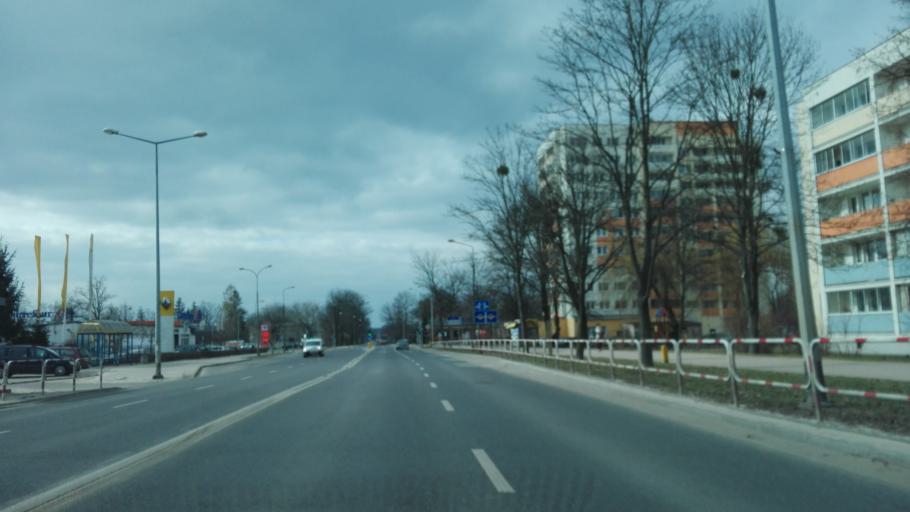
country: PL
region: Lublin Voivodeship
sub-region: Powiat pulawski
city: Pulawy
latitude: 51.4155
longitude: 21.9791
